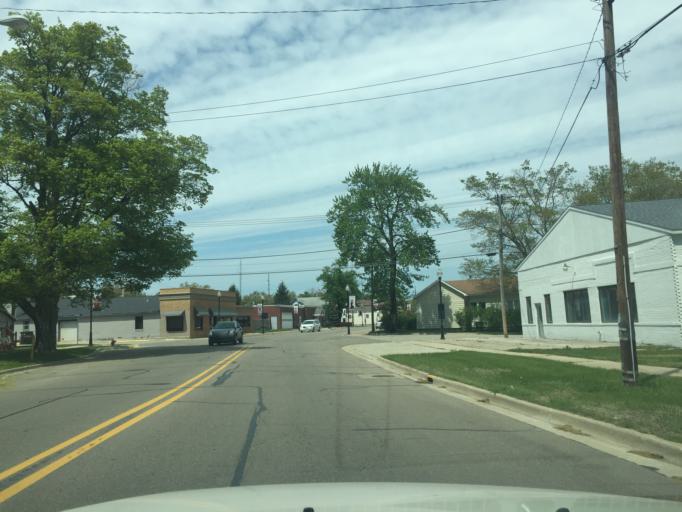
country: US
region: Michigan
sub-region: Berrien County
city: Stevensville
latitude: 42.0121
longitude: -86.5195
